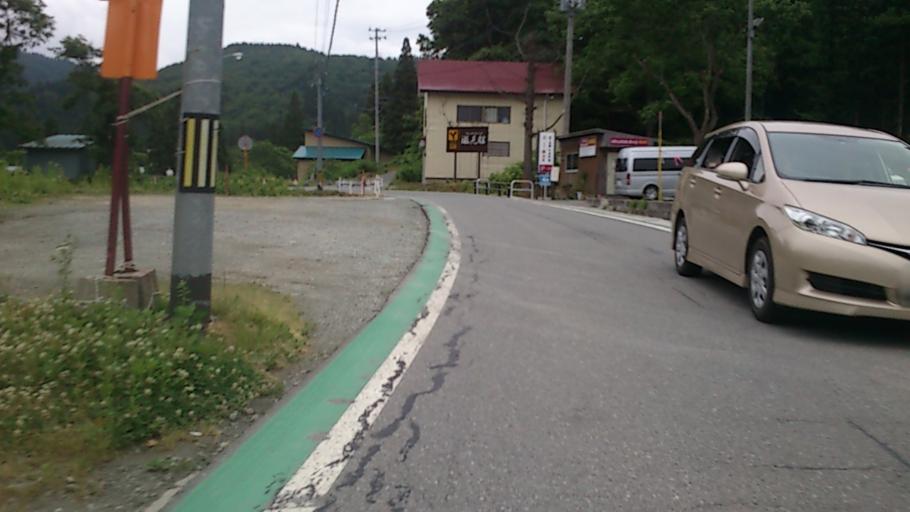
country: JP
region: Yamagata
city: Obanazawa
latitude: 38.5731
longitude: 140.5257
